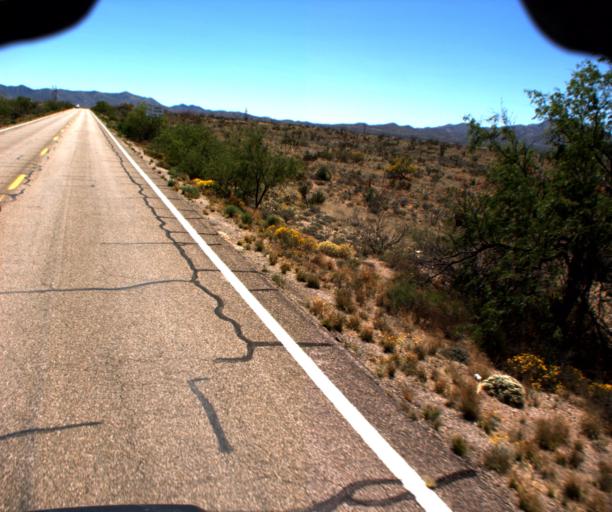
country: US
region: Arizona
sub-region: Pima County
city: Vail
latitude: 31.9961
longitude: -110.6859
